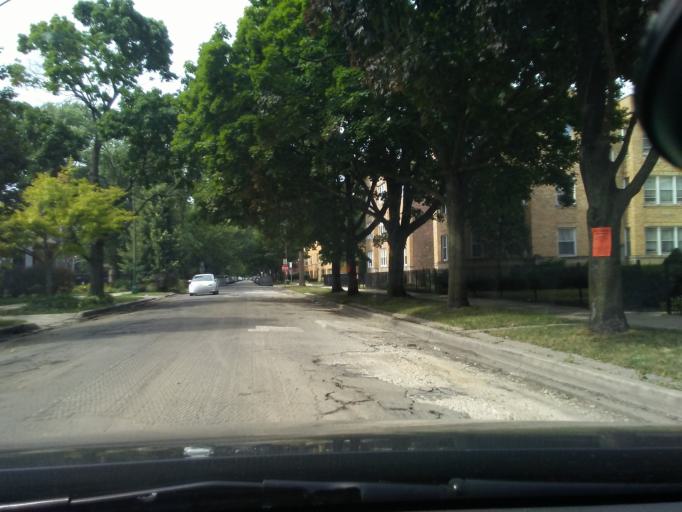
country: US
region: Illinois
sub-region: Cook County
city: Lincolnwood
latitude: 41.9622
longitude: -87.7180
